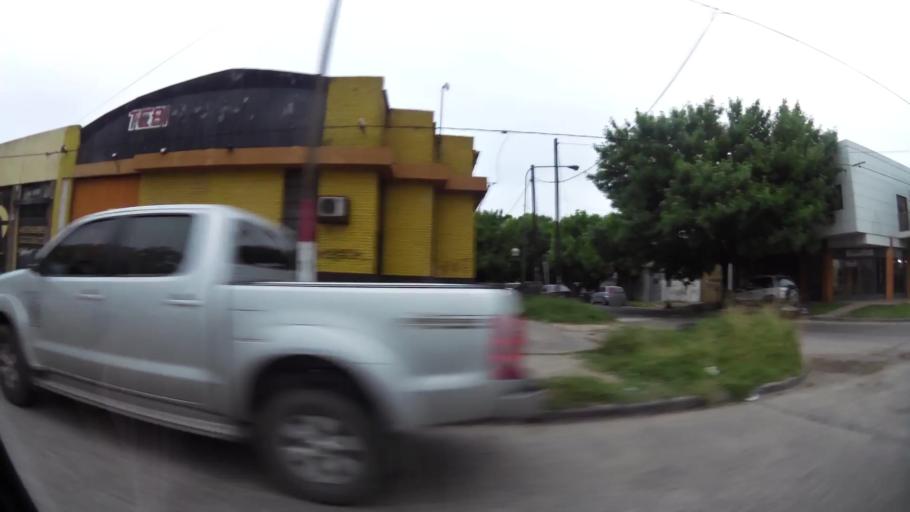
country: AR
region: Buenos Aires
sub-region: Partido de La Plata
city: La Plata
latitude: -34.9146
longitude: -57.9842
